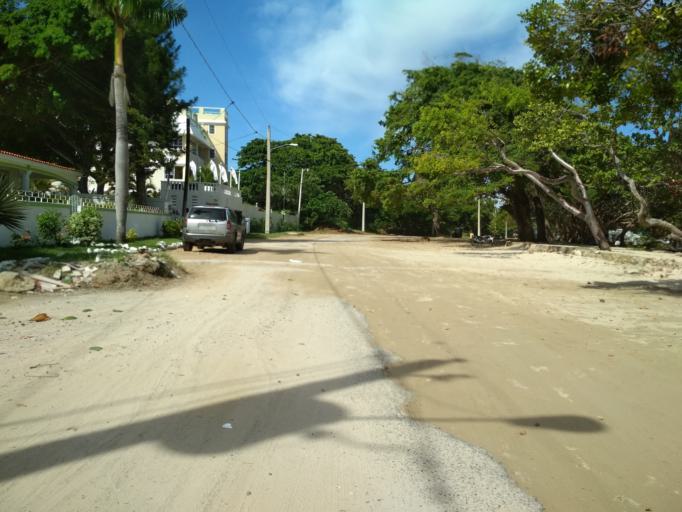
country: DO
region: Puerto Plata
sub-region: Puerto Plata
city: Puerto Plata
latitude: 19.8146
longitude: -70.7153
